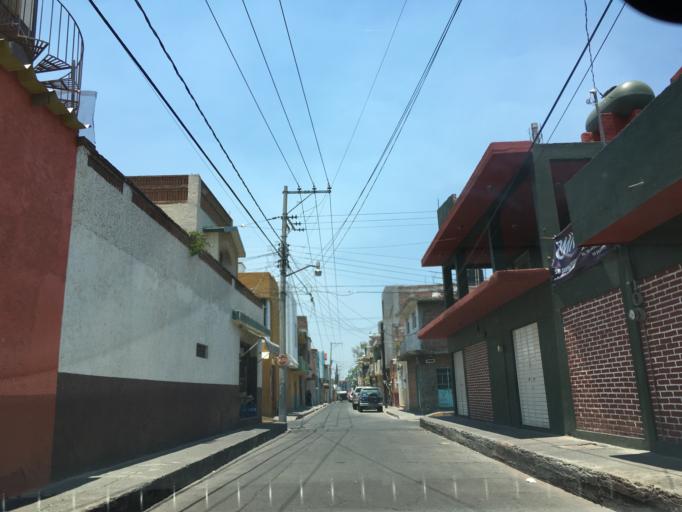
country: MX
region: Guanajuato
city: Moroleon
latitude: 20.1311
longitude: -101.1847
